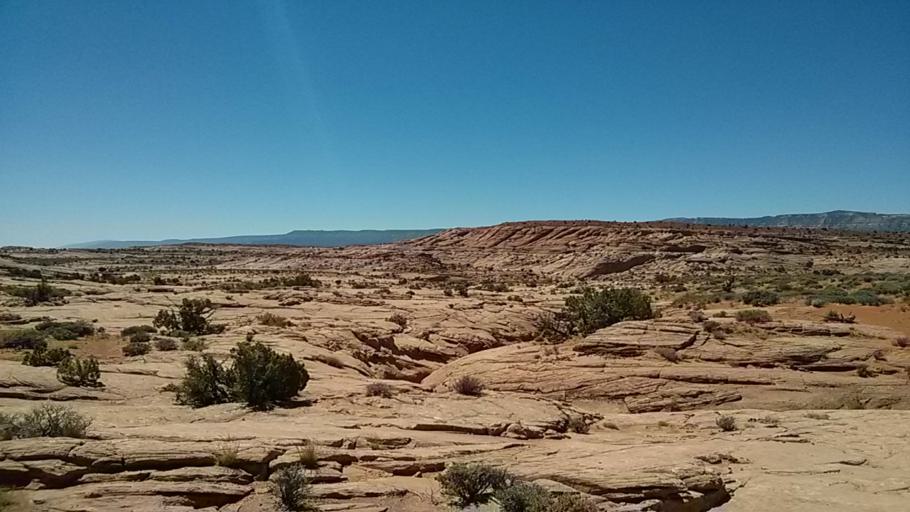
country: US
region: Arizona
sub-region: Coconino County
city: Page
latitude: 37.4854
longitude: -111.2163
